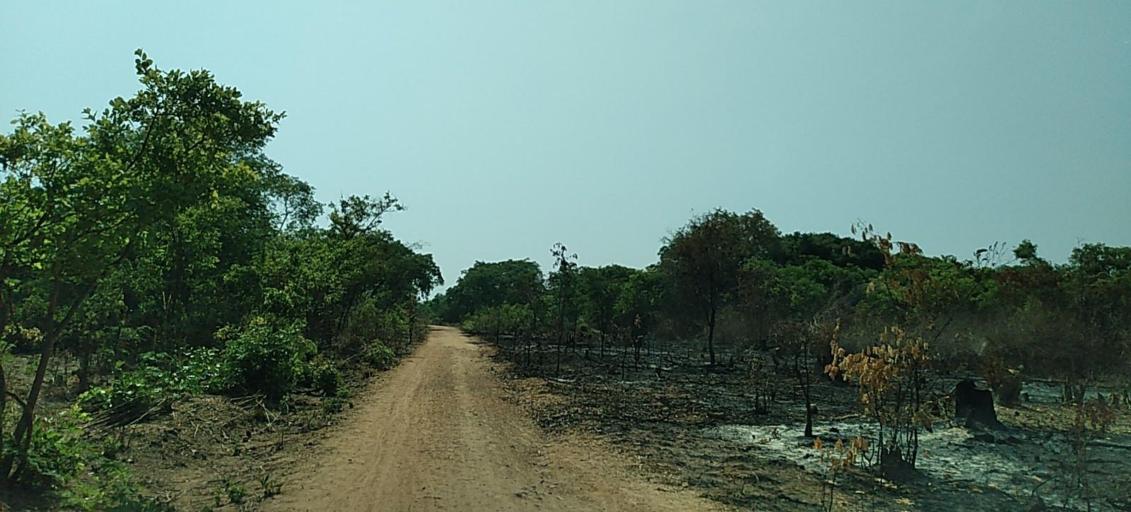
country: ZM
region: Copperbelt
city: Luanshya
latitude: -13.2812
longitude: 28.3164
